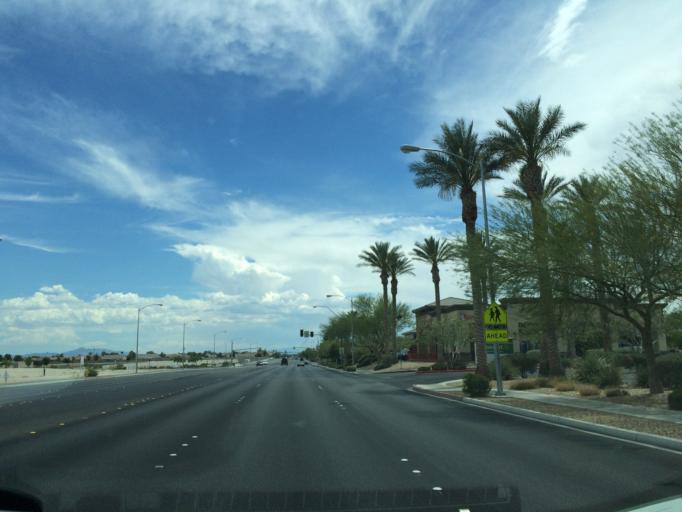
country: US
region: Nevada
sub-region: Clark County
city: North Las Vegas
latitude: 36.2603
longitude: -115.1801
